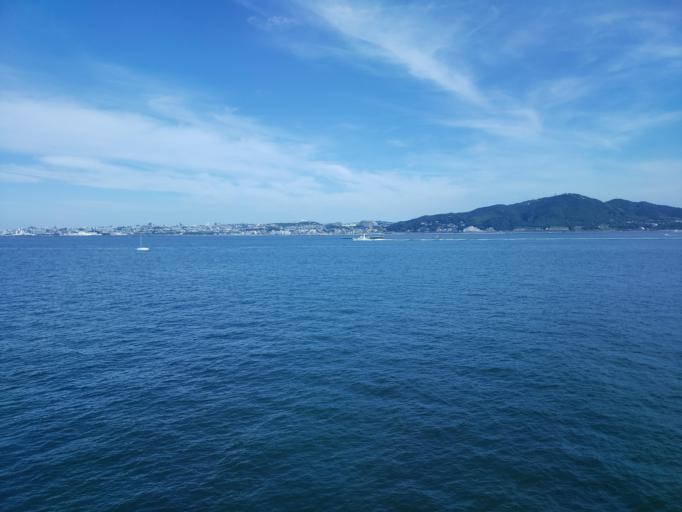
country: JP
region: Hyogo
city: Akashi
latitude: 34.6069
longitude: 135.0984
